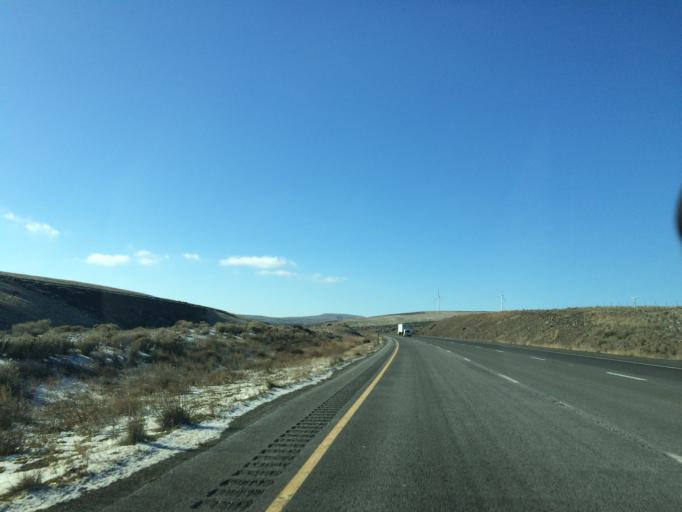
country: US
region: Washington
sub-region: Grant County
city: Mattawa
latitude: 46.9457
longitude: -120.1032
